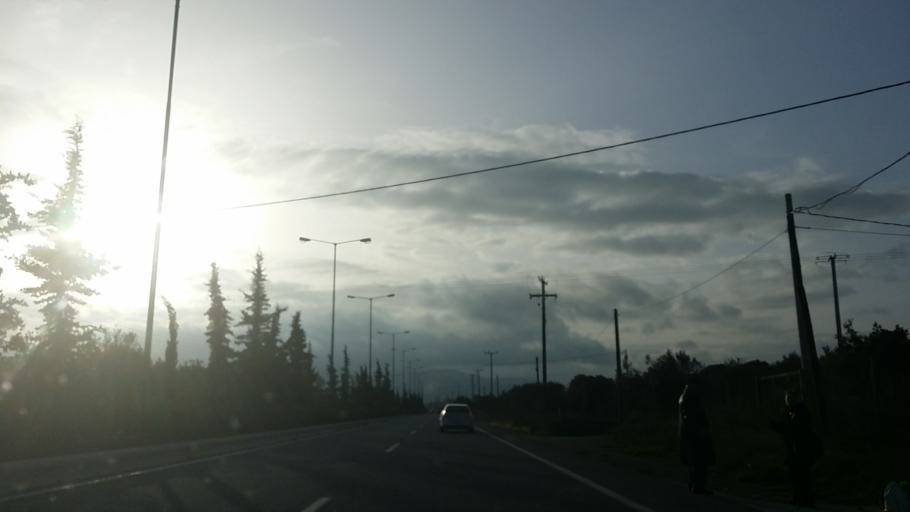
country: GR
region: Attica
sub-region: Nomarchia Anatolikis Attikis
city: Keratea
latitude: 37.8033
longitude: 24.0427
